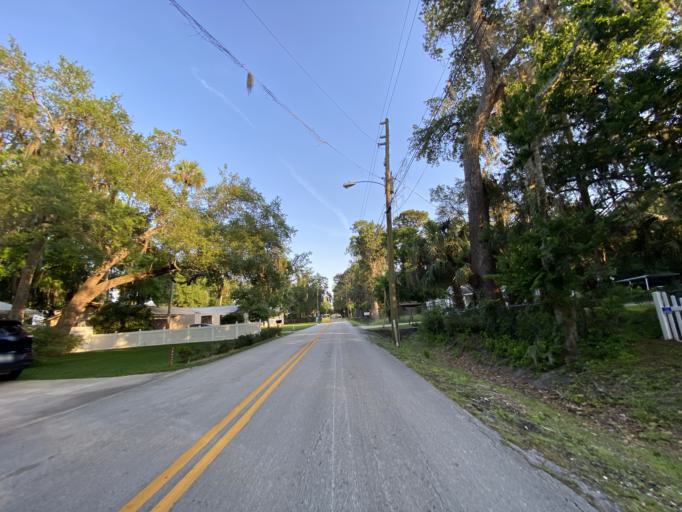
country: US
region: Florida
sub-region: Volusia County
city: Port Orange
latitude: 29.1330
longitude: -81.0058
